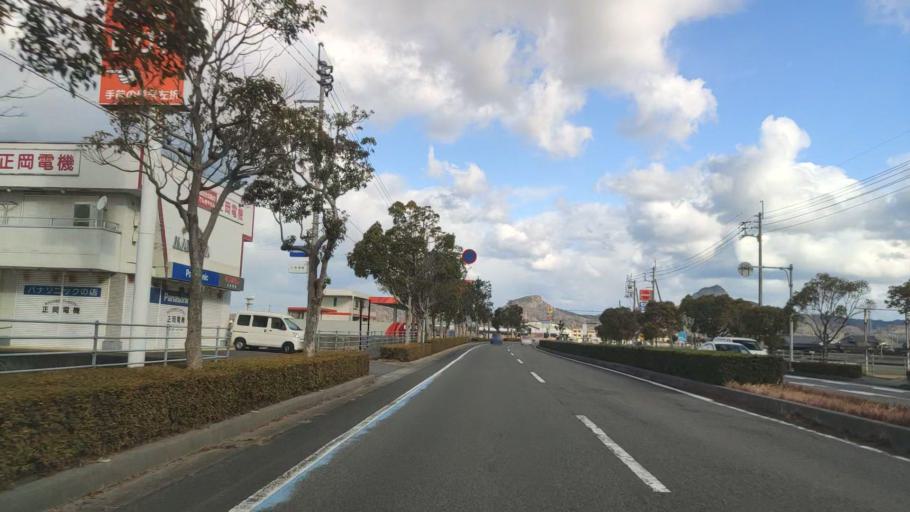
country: JP
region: Ehime
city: Hojo
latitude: 33.9651
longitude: 132.7788
